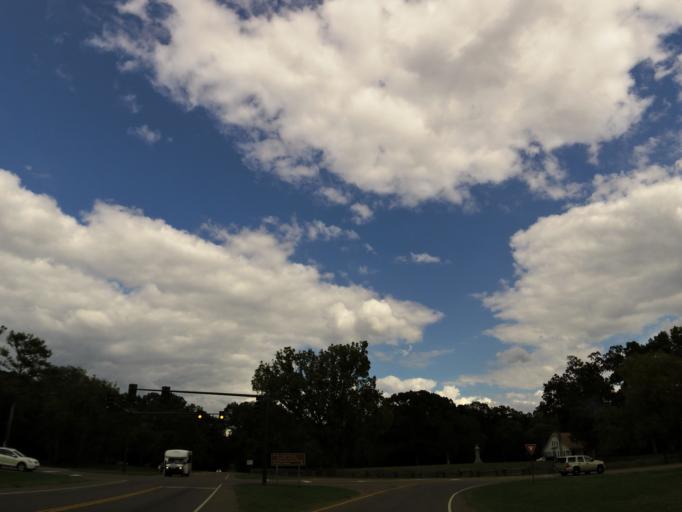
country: US
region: Georgia
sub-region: Catoosa County
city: Fort Oglethorpe
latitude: 34.9416
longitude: -85.2593
